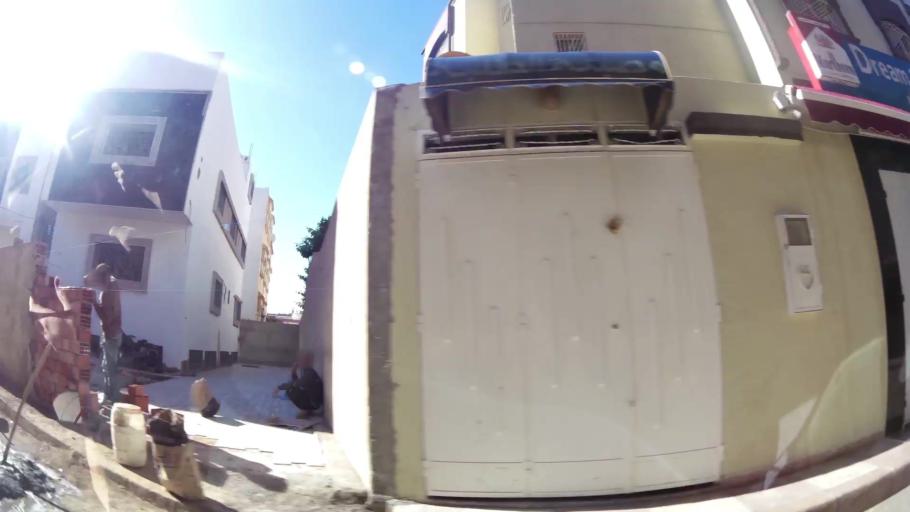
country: MA
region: Oriental
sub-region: Oujda-Angad
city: Oujda
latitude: 34.6548
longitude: -1.8981
